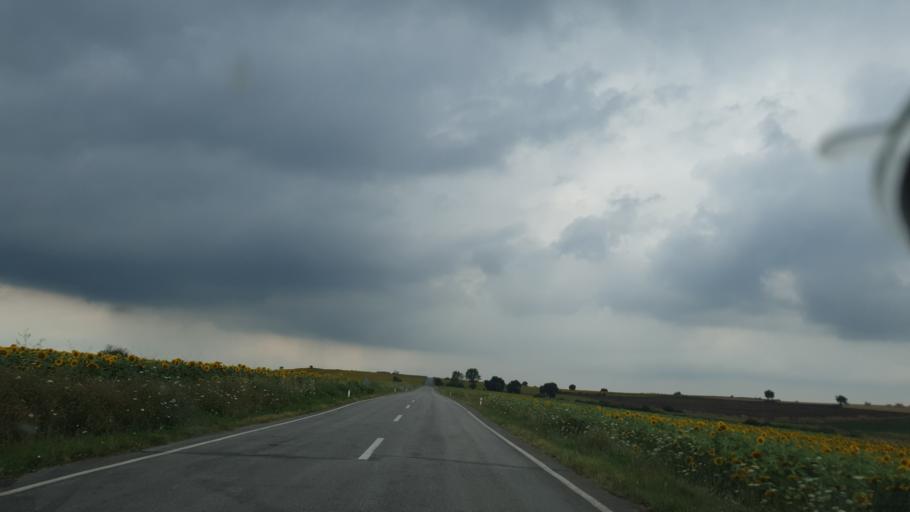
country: TR
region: Tekirdag
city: Hayrabolu
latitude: 41.2181
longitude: 26.9722
